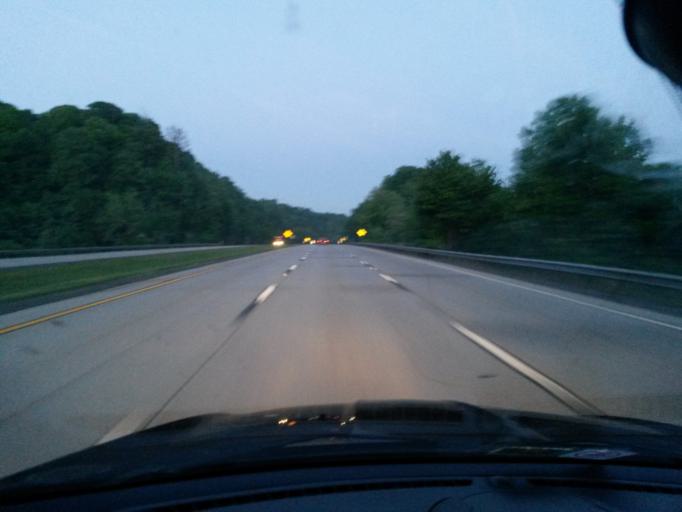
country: US
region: West Virginia
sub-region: Raleigh County
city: Beaver
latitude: 37.7420
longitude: -81.1703
